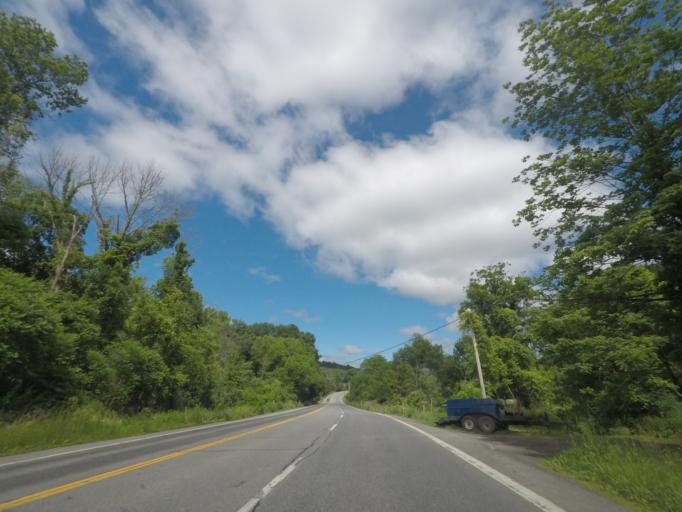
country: US
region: New York
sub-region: Columbia County
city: Philmont
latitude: 42.2092
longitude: -73.6932
